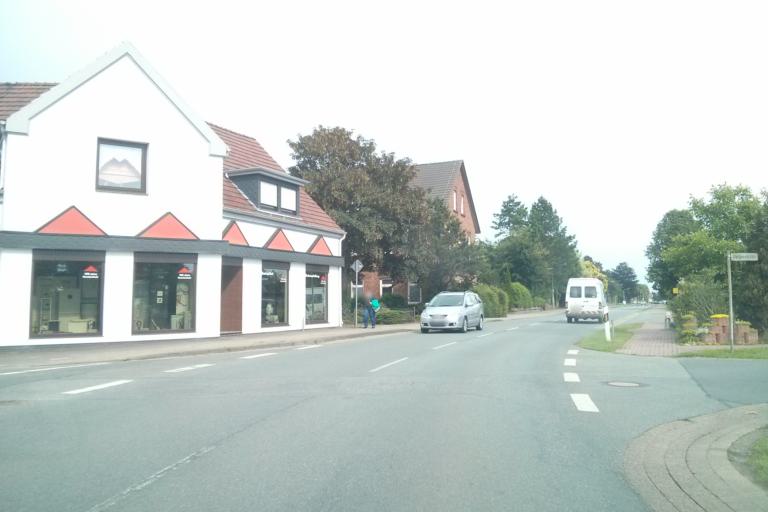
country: DE
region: Lower Saxony
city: Ahsen-Oetzen
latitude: 52.9571
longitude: 9.0787
